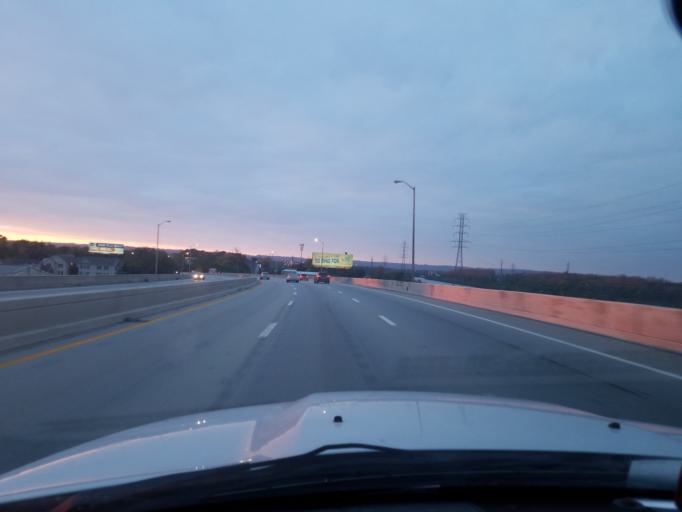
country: US
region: Kentucky
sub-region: Jefferson County
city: Louisville
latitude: 38.2635
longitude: -85.7731
